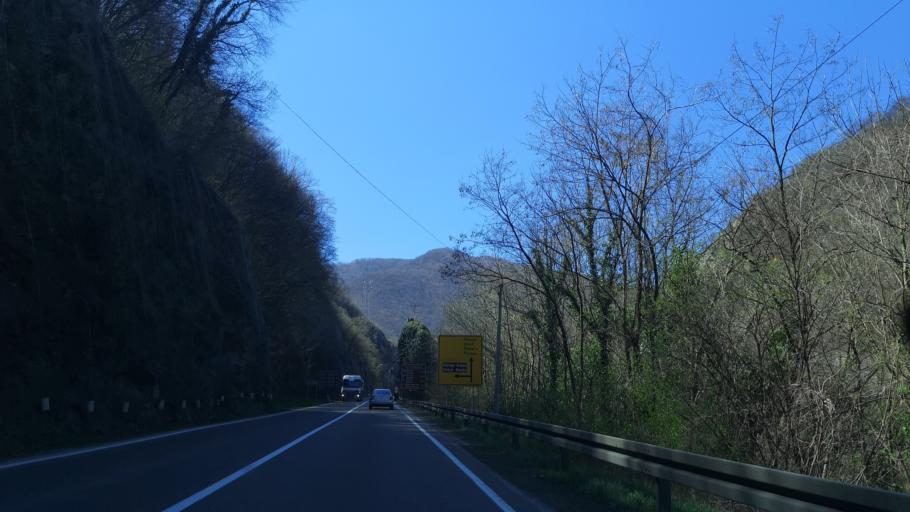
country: RS
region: Central Serbia
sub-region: Moravicki Okrug
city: Lucani
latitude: 43.9030
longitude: 20.1943
